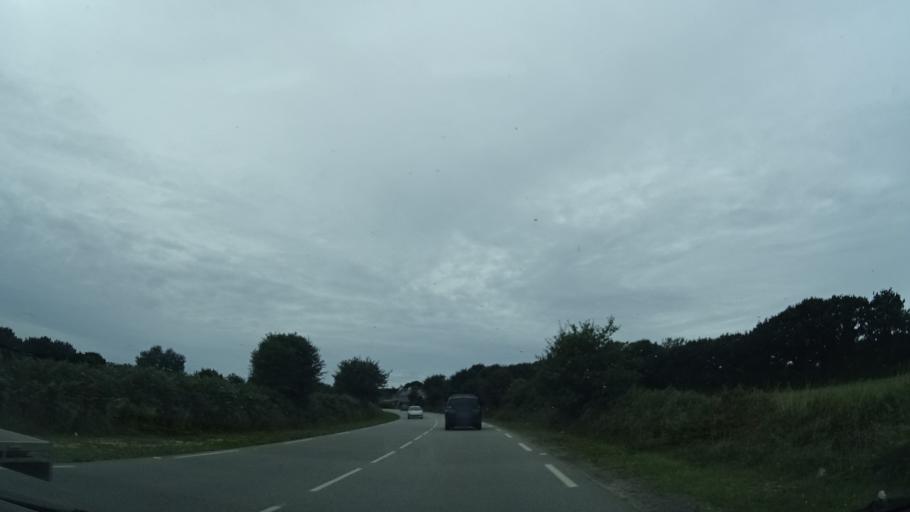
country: FR
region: Brittany
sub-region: Departement du Finistere
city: Saint-Renan
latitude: 48.4308
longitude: -4.6031
